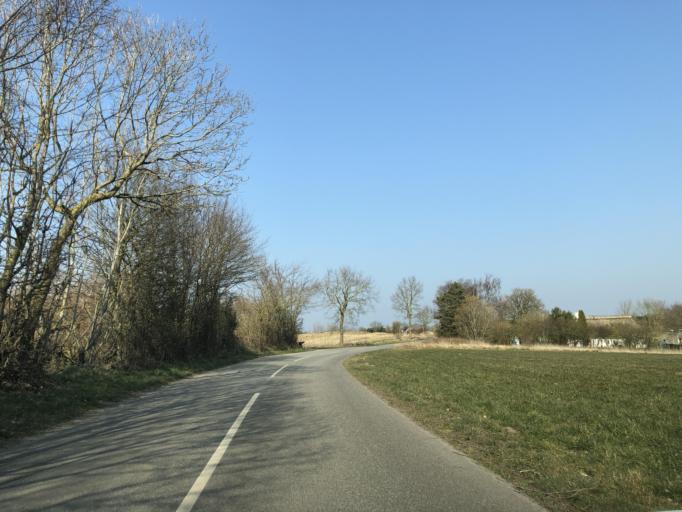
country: DK
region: South Denmark
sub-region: Sonderborg Kommune
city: Nordborg
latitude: 55.0715
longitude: 9.7303
